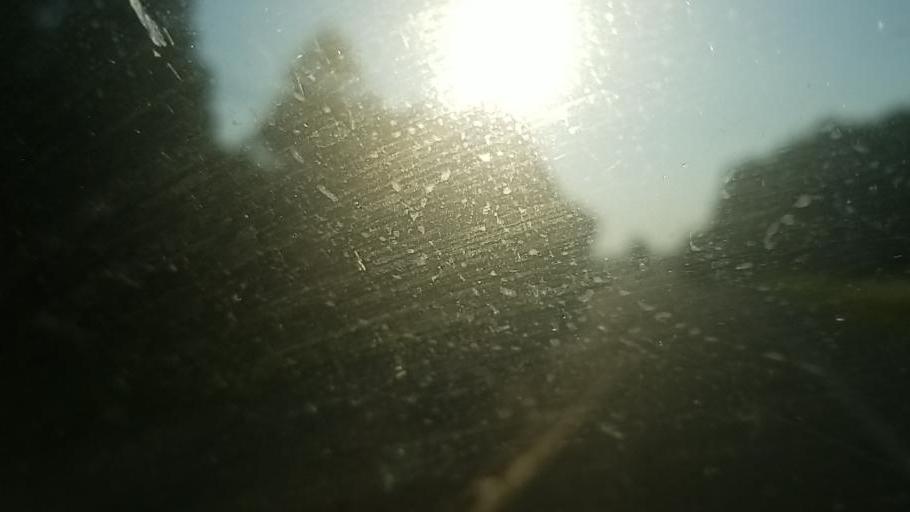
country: US
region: Delaware
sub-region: Sussex County
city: Selbyville
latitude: 38.4632
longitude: -75.1599
